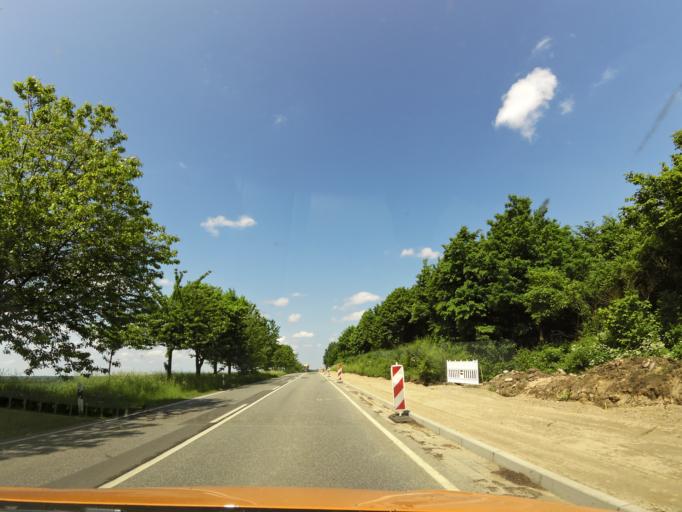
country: DE
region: Mecklenburg-Vorpommern
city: Gadebusch
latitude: 53.6801
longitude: 11.1404
